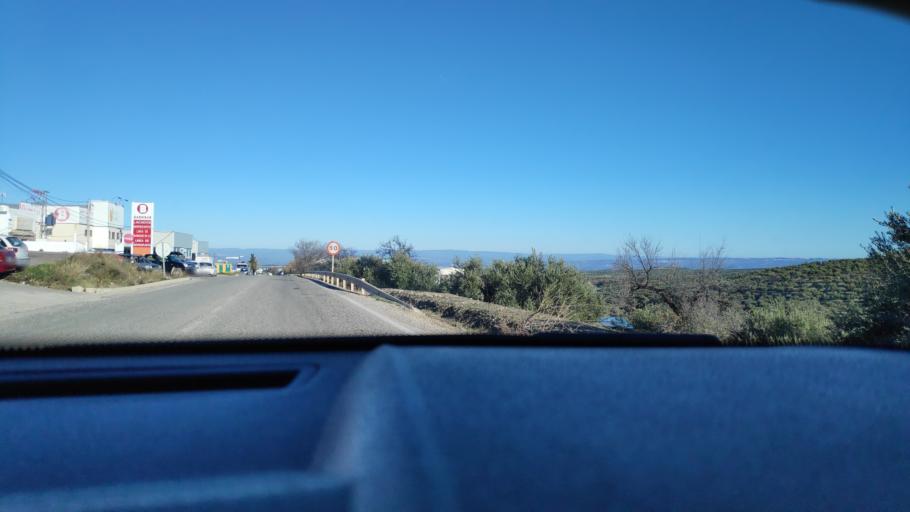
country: ES
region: Andalusia
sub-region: Provincia de Jaen
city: Mancha Real
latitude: 37.7989
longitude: -3.6093
